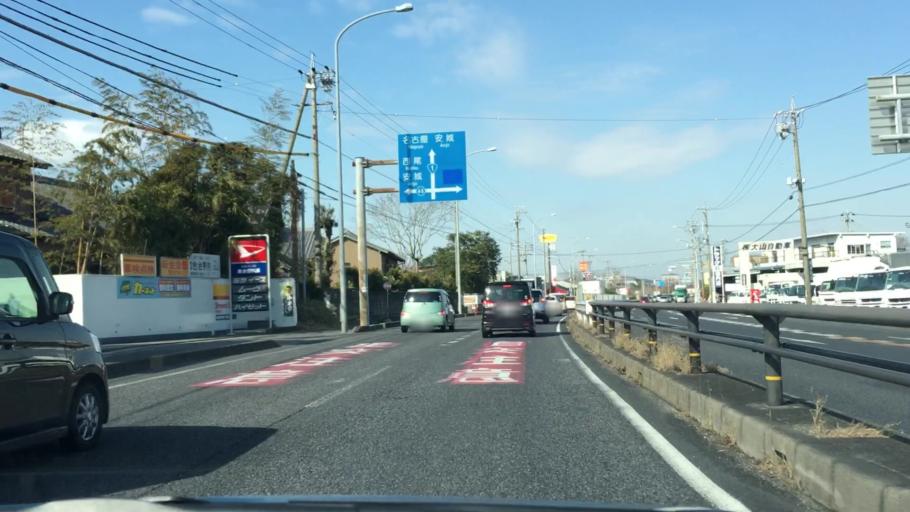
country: JP
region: Aichi
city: Okazaki
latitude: 34.9289
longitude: 137.1984
